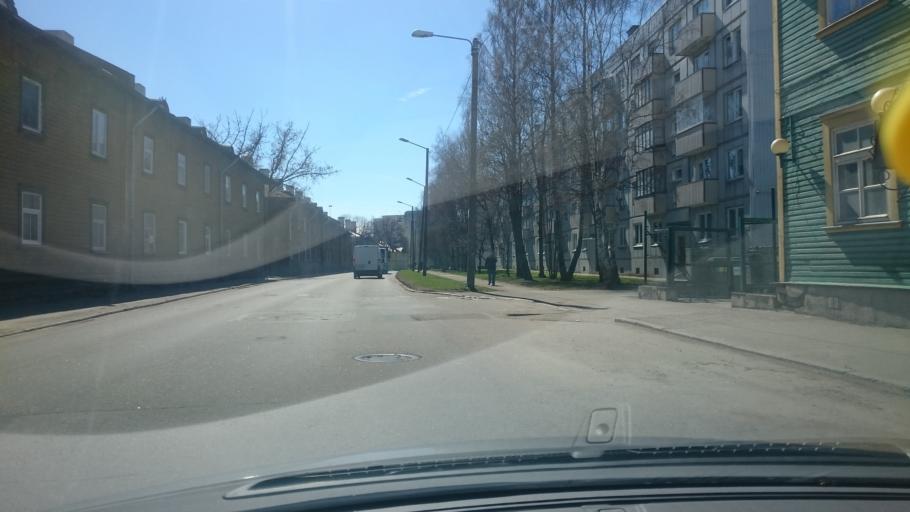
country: EE
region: Harju
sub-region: Tallinna linn
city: Tallinn
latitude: 59.4517
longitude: 24.7019
